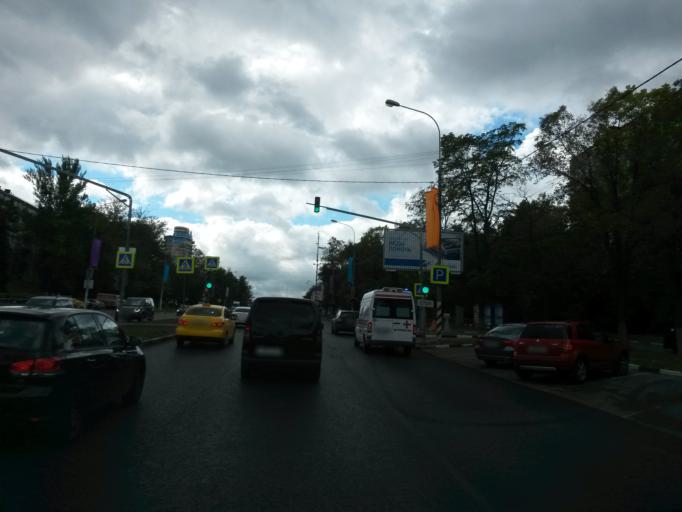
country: RU
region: Moskovskaya
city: Cheremushki
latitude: 55.6748
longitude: 37.5594
